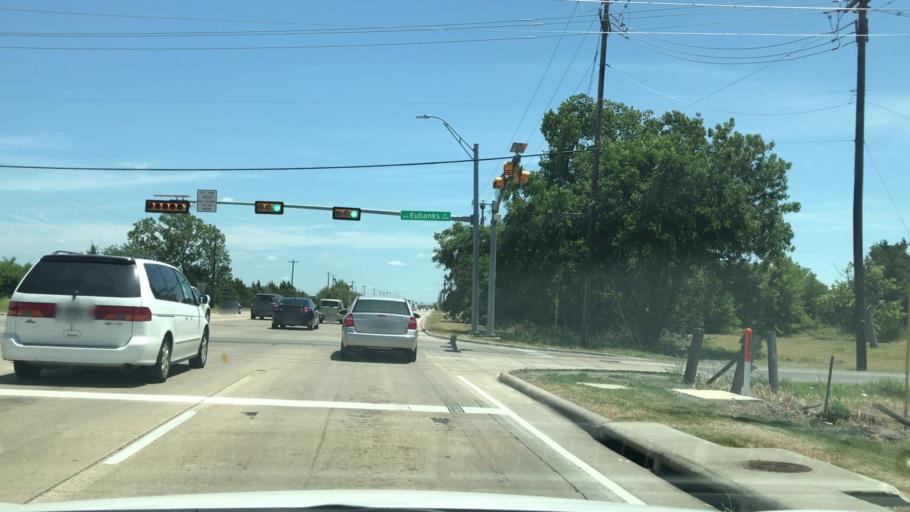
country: US
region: Texas
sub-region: Collin County
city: Wylie
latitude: 33.0229
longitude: -96.5196
